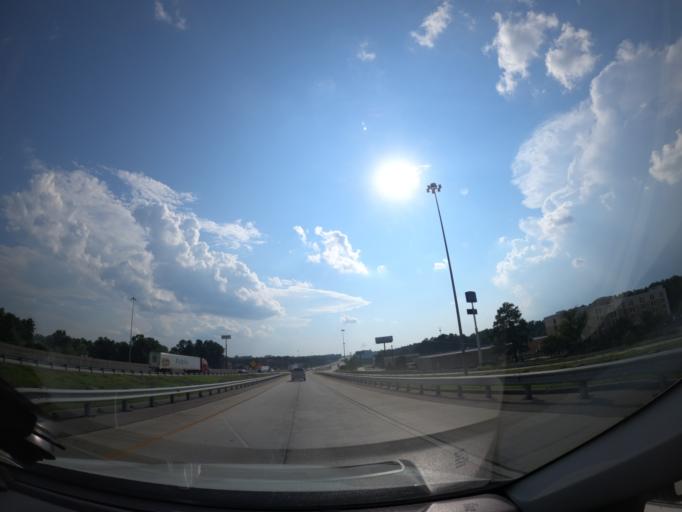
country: US
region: Georgia
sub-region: Columbia County
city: Martinez
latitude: 33.4934
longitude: -82.0860
